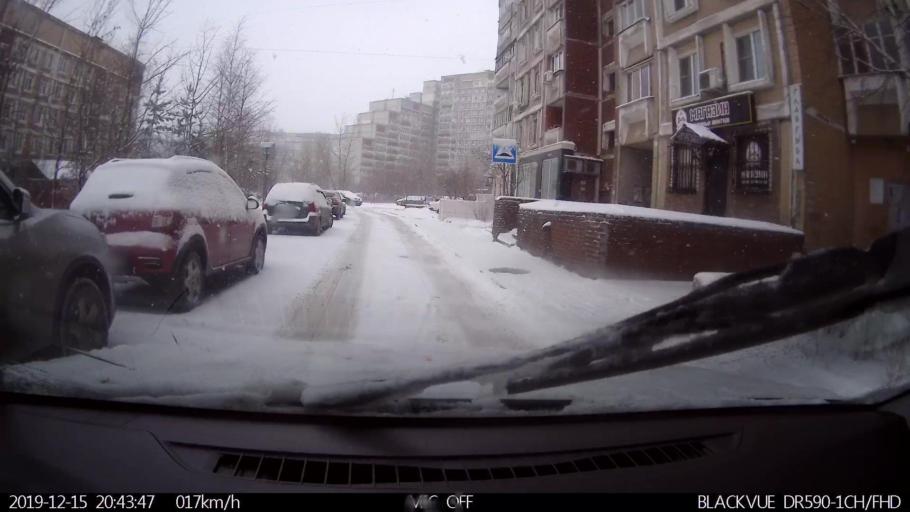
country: RU
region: Nizjnij Novgorod
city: Nizhniy Novgorod
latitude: 56.3427
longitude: 43.9416
